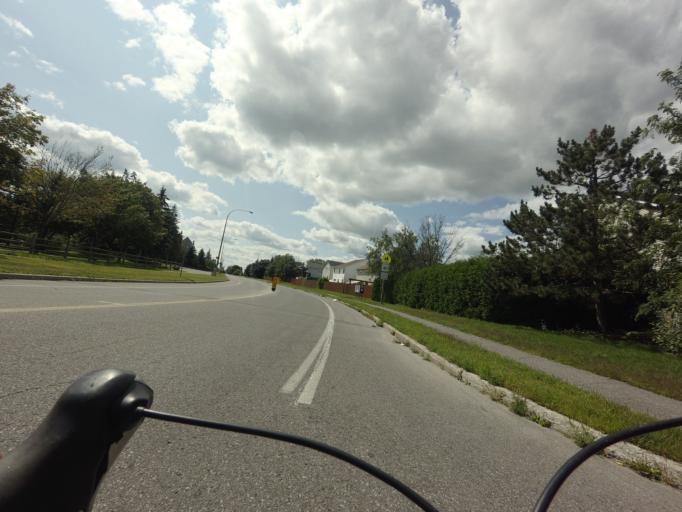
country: CA
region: Ontario
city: Bells Corners
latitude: 45.3011
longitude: -75.8556
